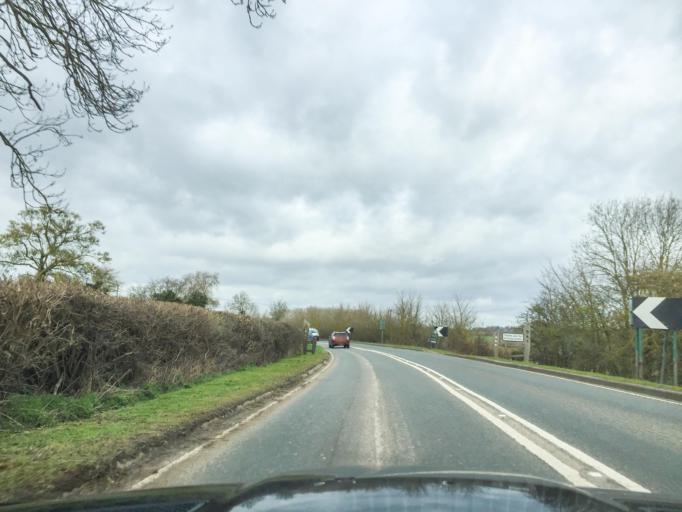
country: GB
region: England
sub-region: Warwickshire
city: Shipston on Stour
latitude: 52.0698
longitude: -1.6197
